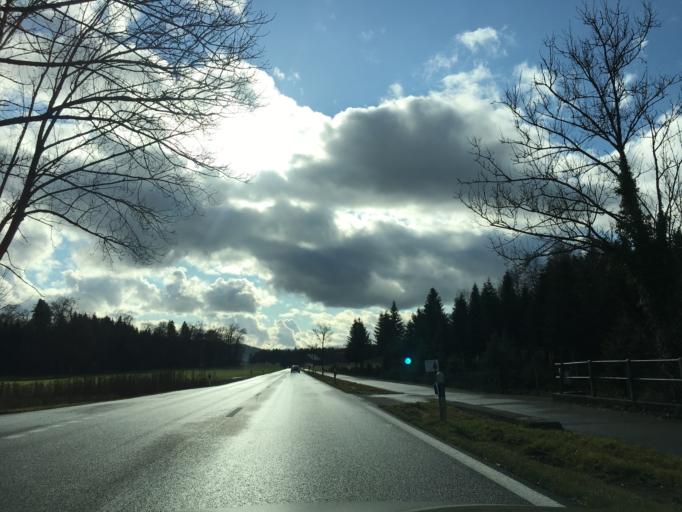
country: CH
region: Aargau
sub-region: Bezirk Muri
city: Oberruti
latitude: 47.1726
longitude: 8.3941
